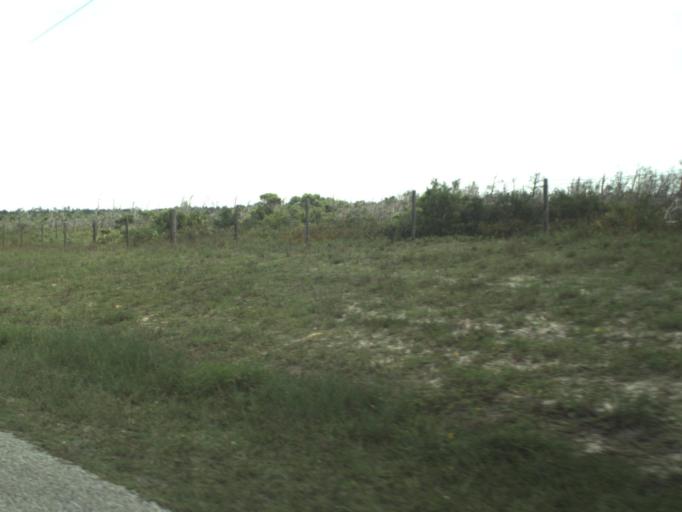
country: US
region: Florida
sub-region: Martin County
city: Hobe Sound
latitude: 27.0410
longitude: -80.1142
